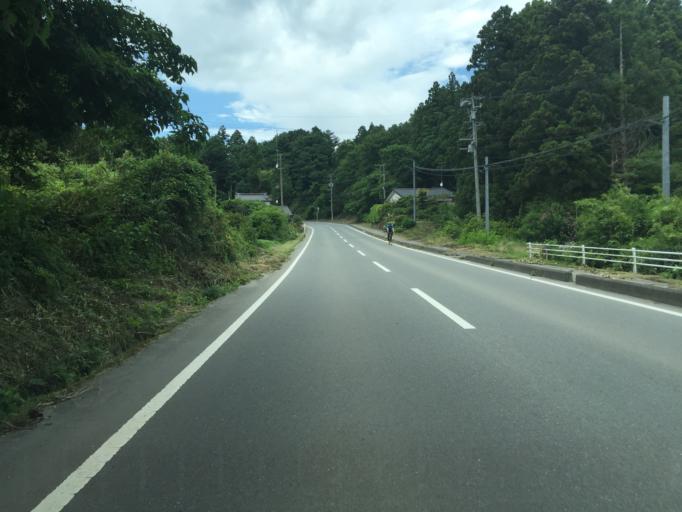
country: JP
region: Miyagi
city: Marumori
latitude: 37.7558
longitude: 140.9160
